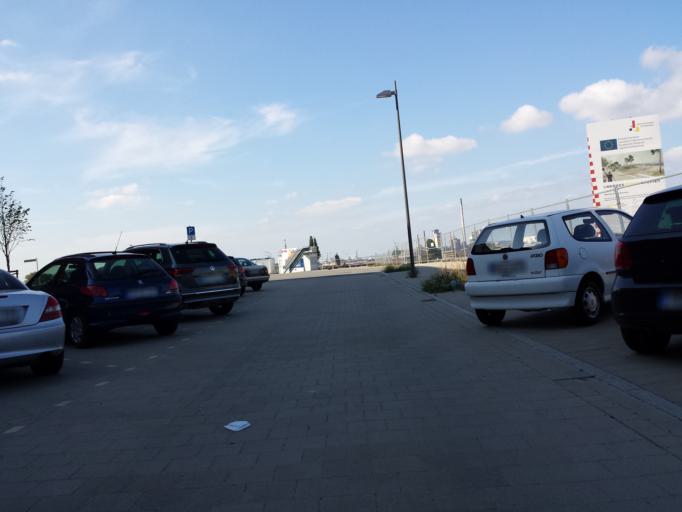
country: DE
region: Bremen
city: Bremen
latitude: 53.1027
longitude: 8.7537
